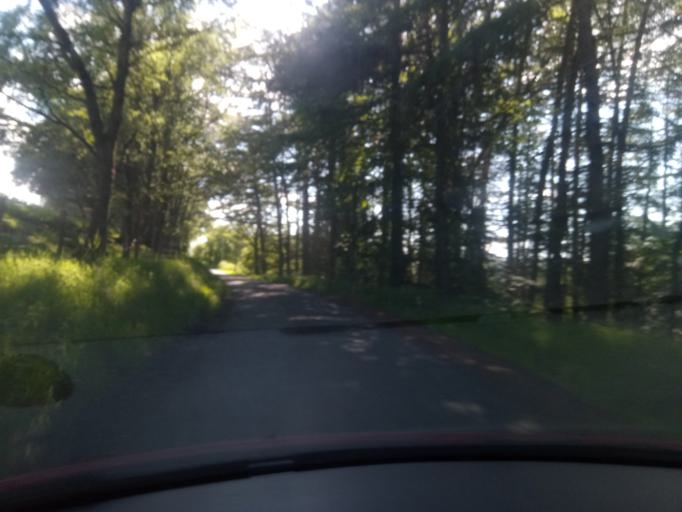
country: GB
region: Scotland
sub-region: The Scottish Borders
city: Innerleithen
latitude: 55.5103
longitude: -3.0984
